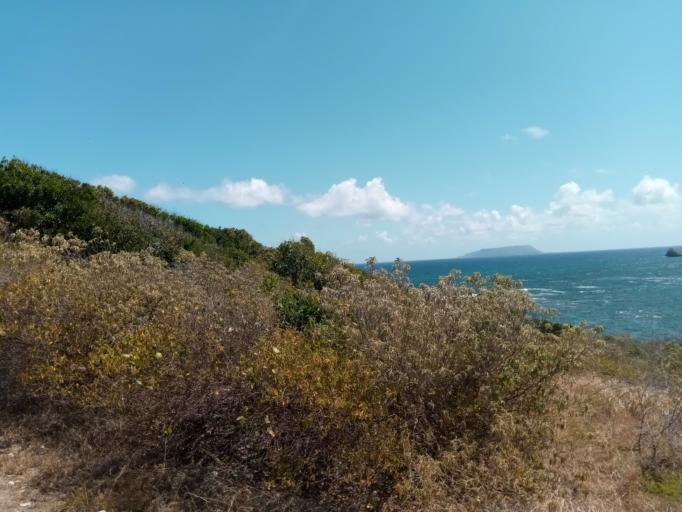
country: GP
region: Guadeloupe
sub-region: Guadeloupe
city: Saint-Francois
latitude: 16.2620
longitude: -61.2191
